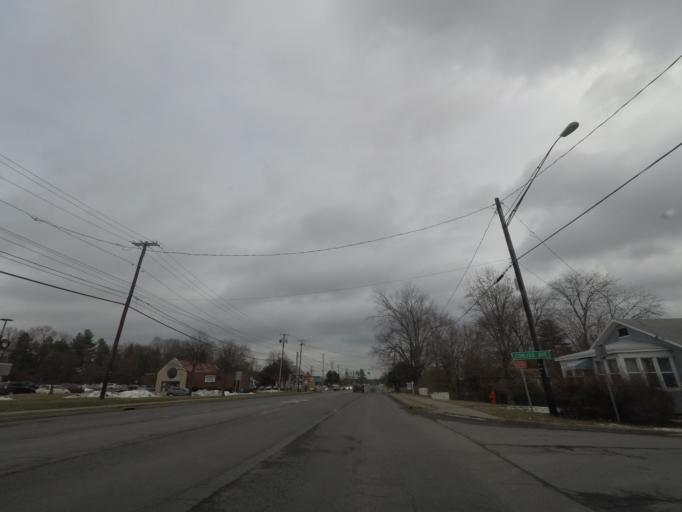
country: US
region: New York
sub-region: Rensselaer County
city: Hampton Manor
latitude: 42.6055
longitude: -73.7193
